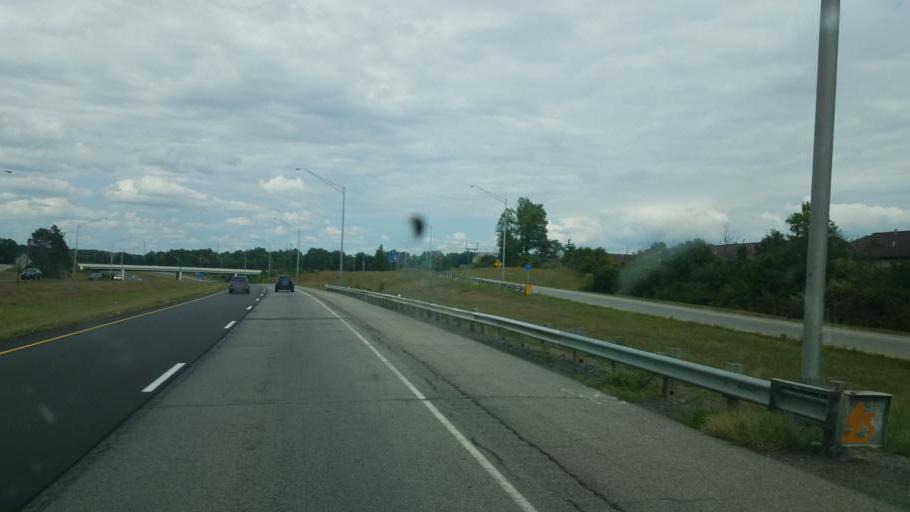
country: US
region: Ohio
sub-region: Mahoning County
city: Austintown
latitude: 41.0963
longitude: -80.7512
